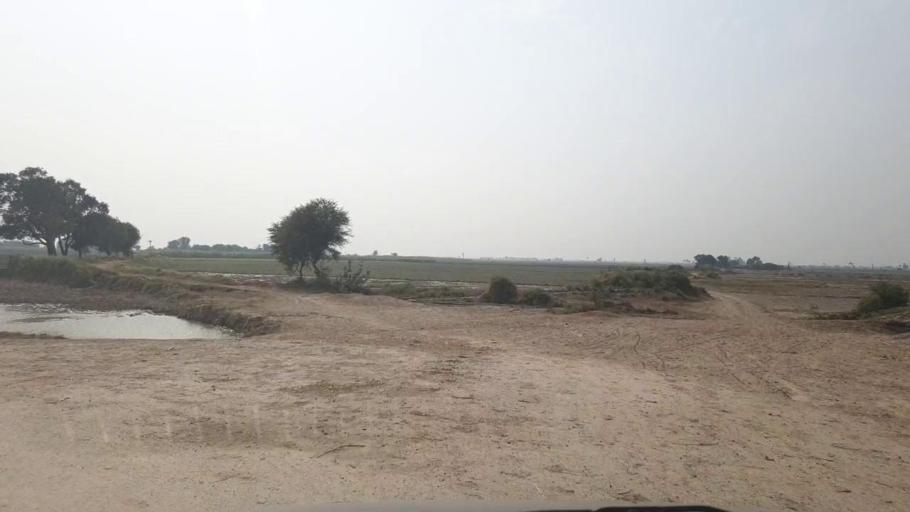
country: PK
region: Sindh
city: Tando Muhammad Khan
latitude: 25.1107
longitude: 68.3849
